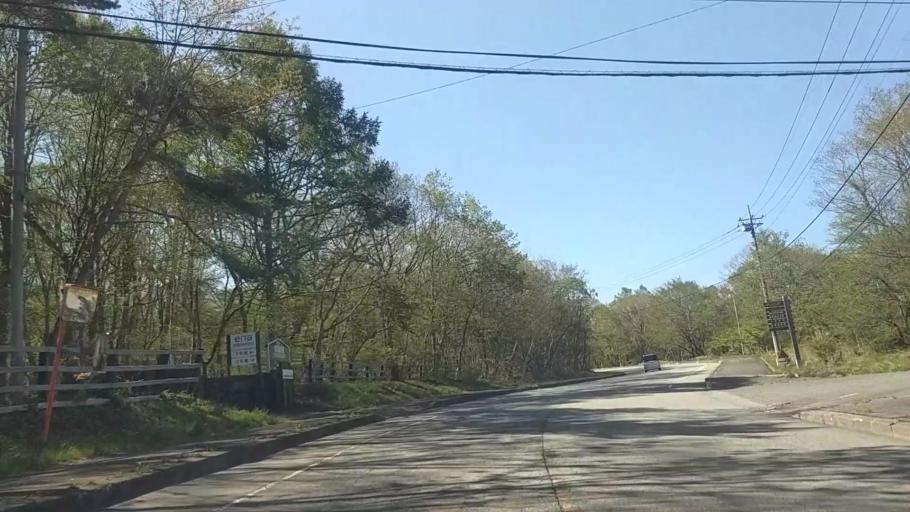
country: JP
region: Yamanashi
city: Nirasaki
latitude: 35.9378
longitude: 138.4415
